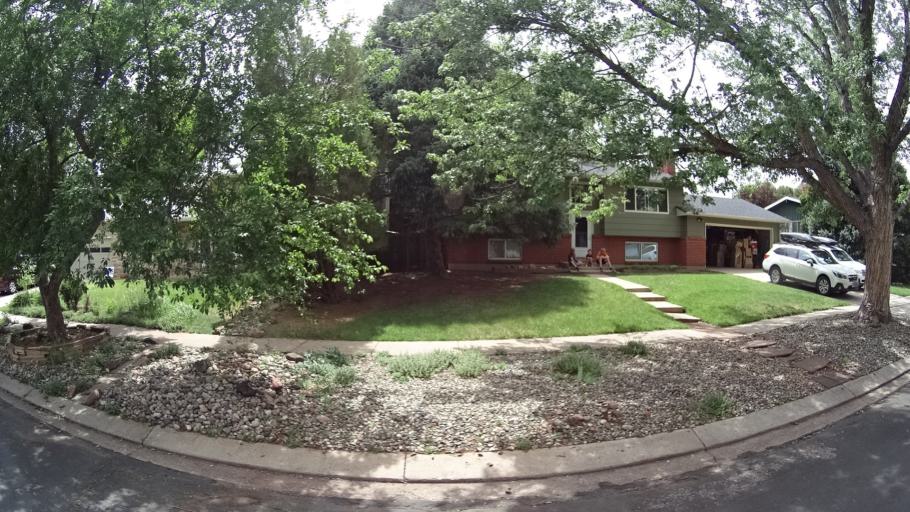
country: US
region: Colorado
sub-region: El Paso County
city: Manitou Springs
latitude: 38.8705
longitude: -104.8713
